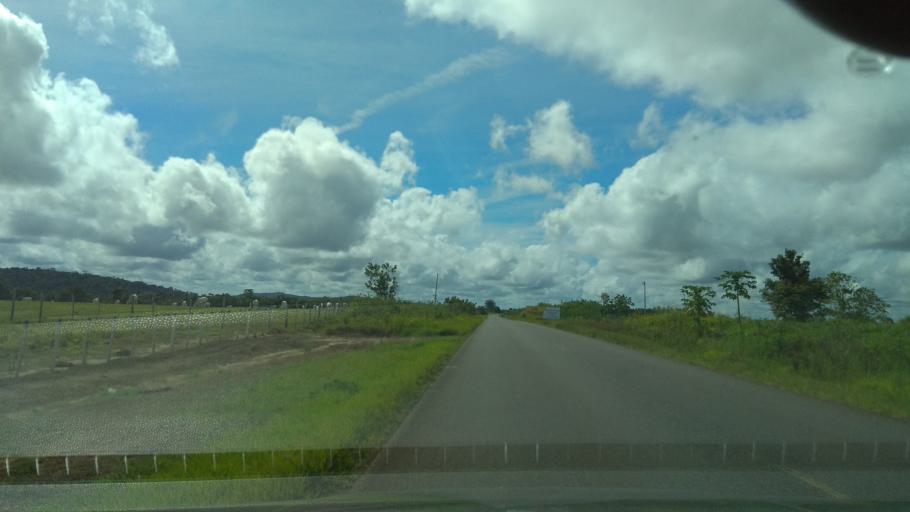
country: BR
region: Bahia
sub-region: Mutuipe
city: Mutuipe
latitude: -13.1687
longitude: -39.3454
